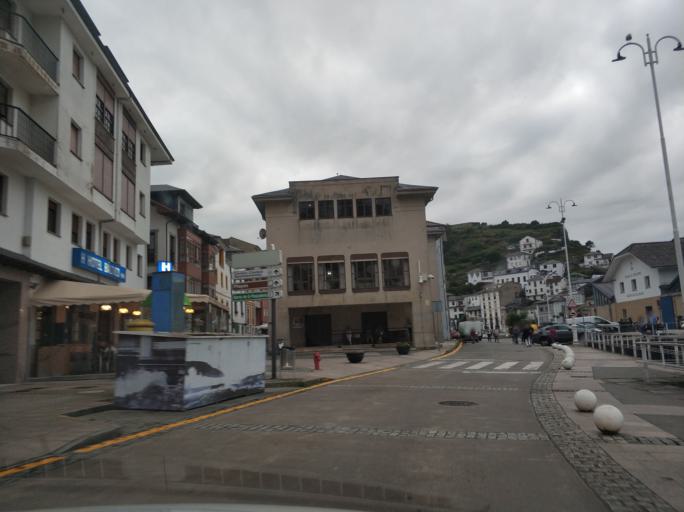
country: ES
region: Asturias
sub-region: Province of Asturias
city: Navia
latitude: 43.5451
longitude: -6.5328
